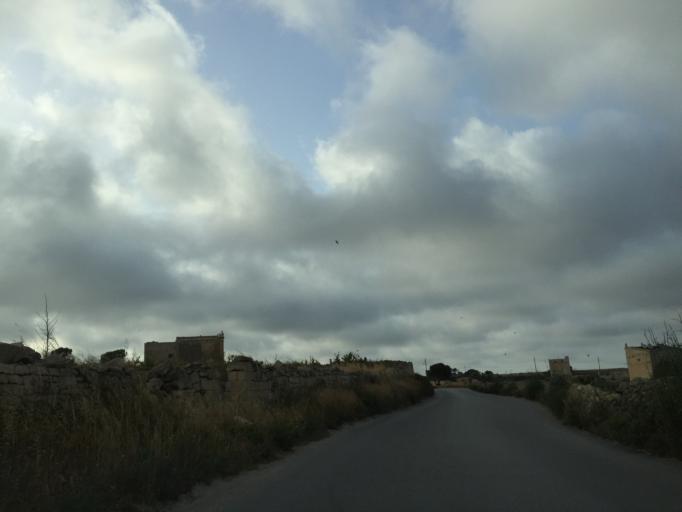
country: MT
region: Is-Siggiewi
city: Siggiewi
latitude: 35.8650
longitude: 14.4174
